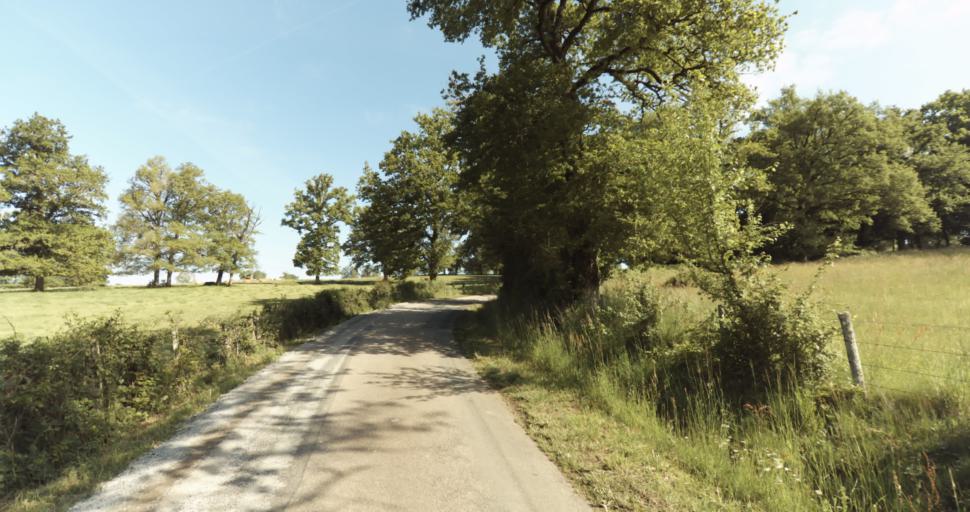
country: FR
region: Limousin
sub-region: Departement de la Haute-Vienne
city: Solignac
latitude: 45.7004
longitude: 1.2551
